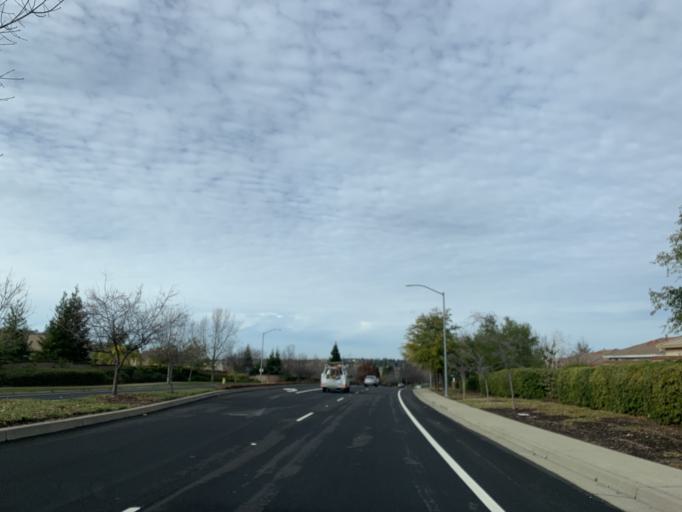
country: US
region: California
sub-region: El Dorado County
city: El Dorado Hills
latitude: 38.6727
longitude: -121.1009
